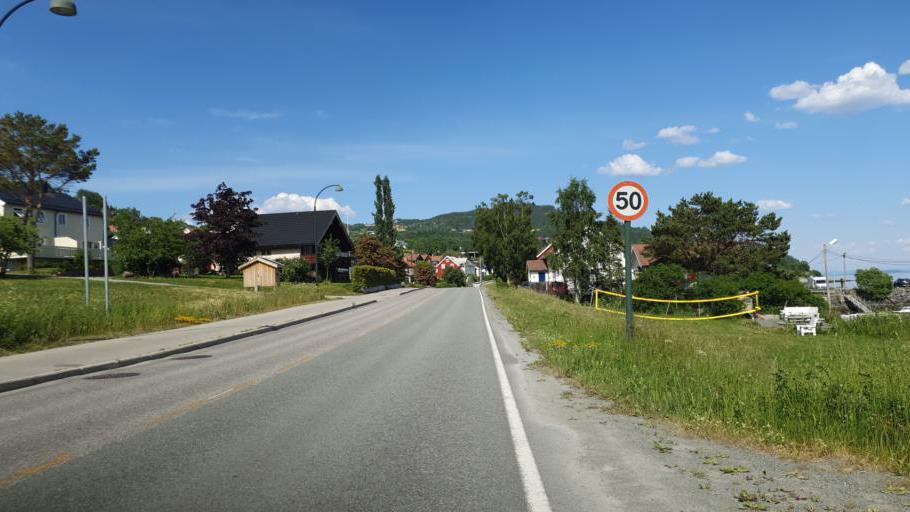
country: NO
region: Nord-Trondelag
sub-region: Leksvik
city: Leksvik
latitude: 63.6696
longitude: 10.6173
